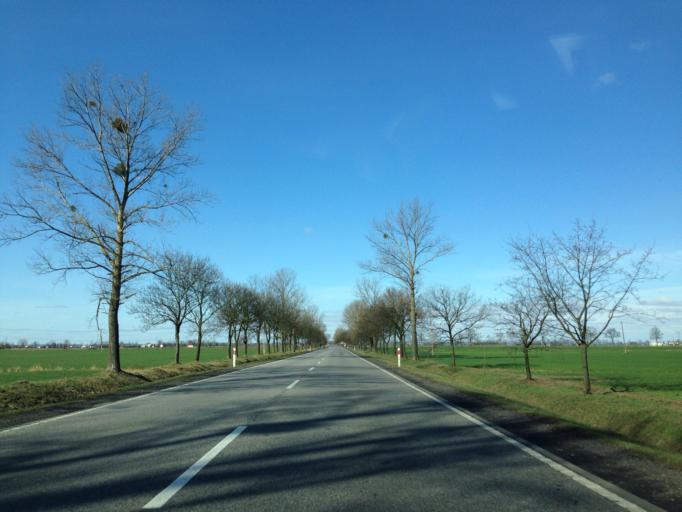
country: PL
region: Pomeranian Voivodeship
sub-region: Powiat malborski
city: Malbork
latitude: 54.0468
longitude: 18.9687
